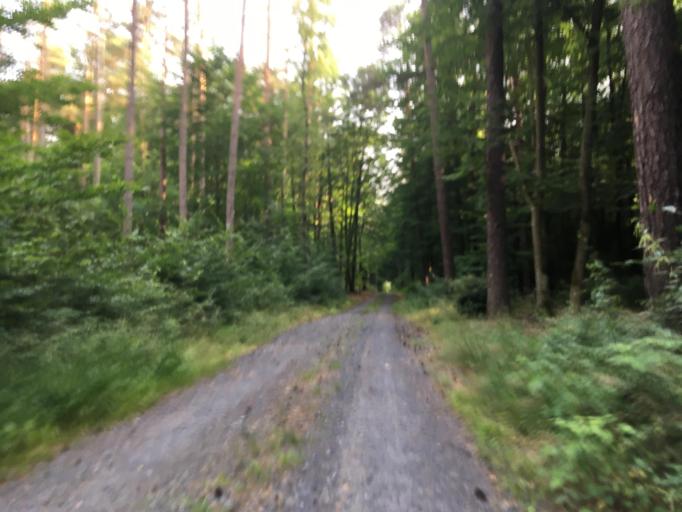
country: DE
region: Brandenburg
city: Wandlitz
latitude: 52.7328
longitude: 13.5307
